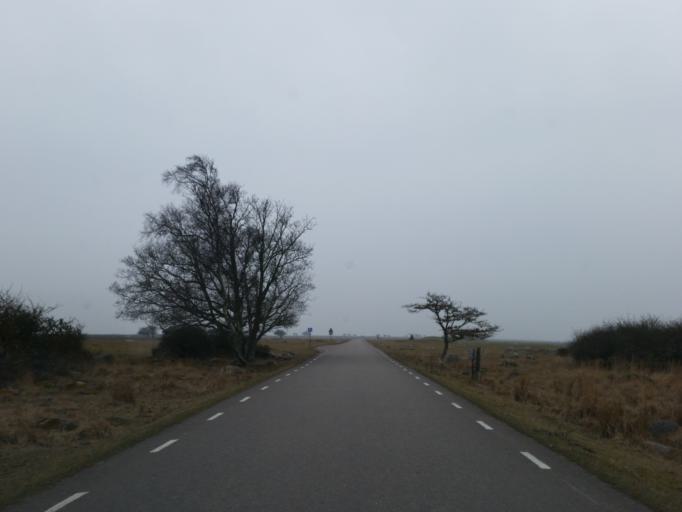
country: SE
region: Kalmar
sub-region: Morbylanga Kommun
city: Moerbylanga
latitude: 56.2125
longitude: 16.4072
